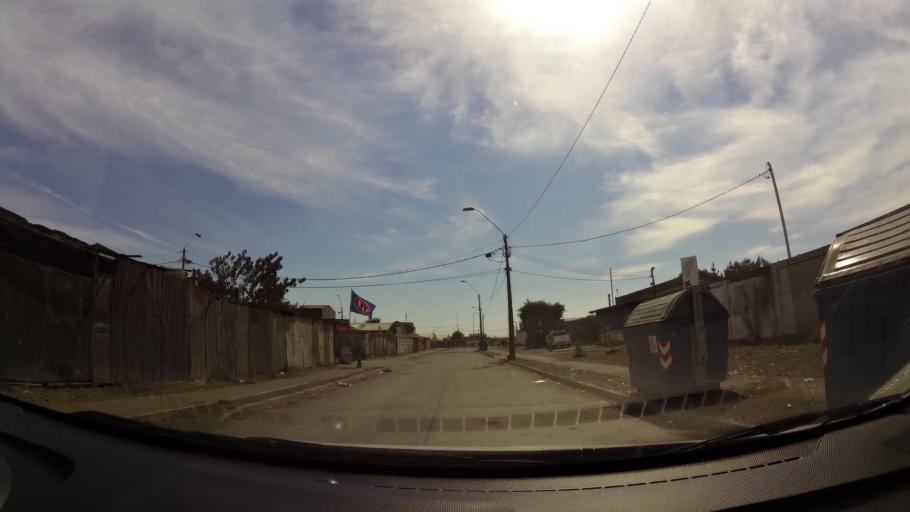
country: CL
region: Biobio
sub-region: Provincia de Concepcion
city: Talcahuano
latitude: -36.7350
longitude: -73.1139
